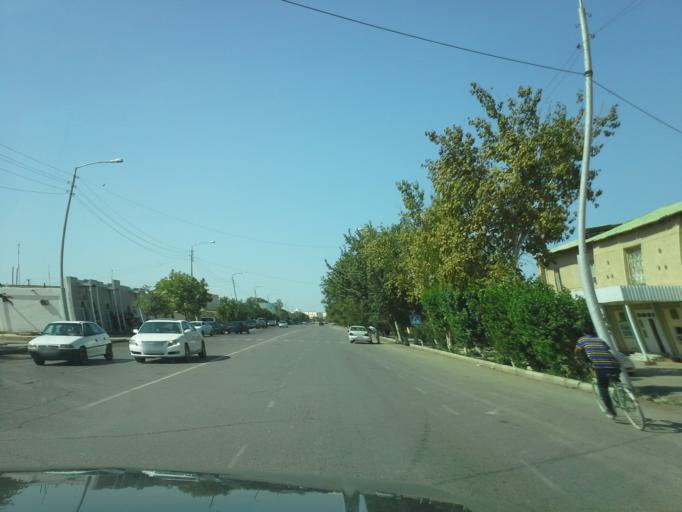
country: TM
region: Dasoguz
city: Dasoguz
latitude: 41.8194
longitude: 59.9821
